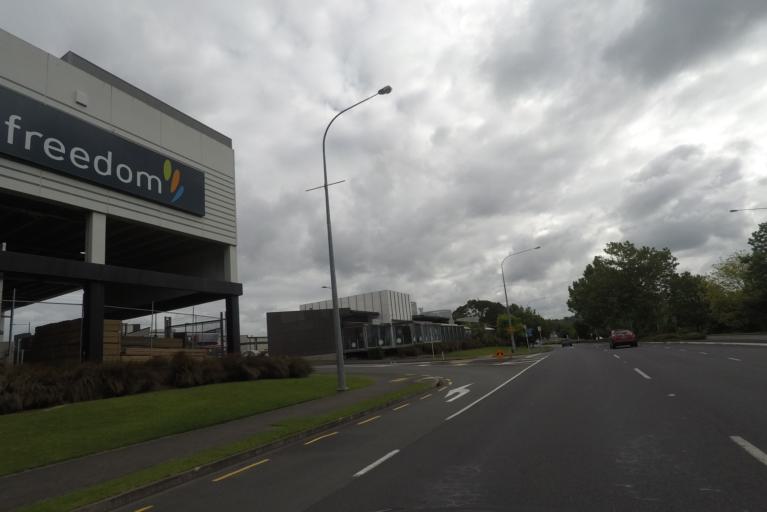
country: NZ
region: Auckland
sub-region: Auckland
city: Rothesay Bay
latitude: -36.7222
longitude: 174.7054
